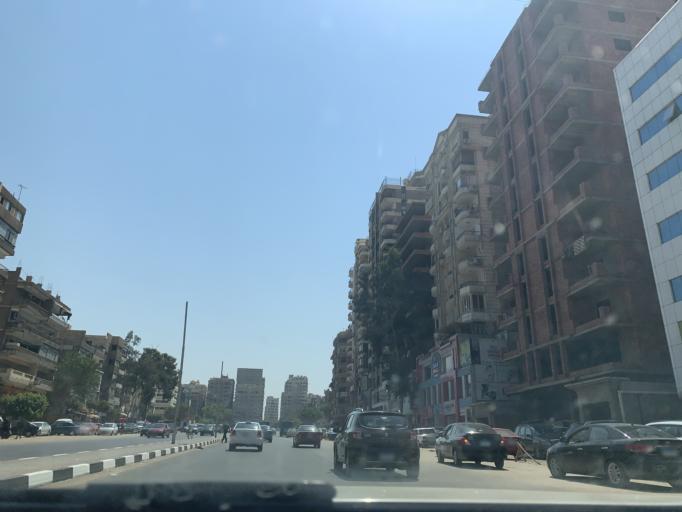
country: EG
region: Muhafazat al Qahirah
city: Cairo
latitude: 30.0526
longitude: 31.3464
